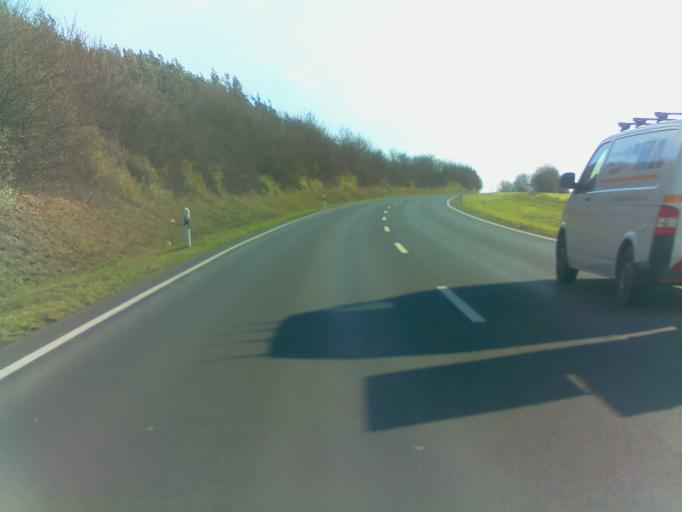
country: DE
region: Bavaria
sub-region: Regierungsbezirk Unterfranken
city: Grosseibstadt
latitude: 50.3079
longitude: 10.3894
